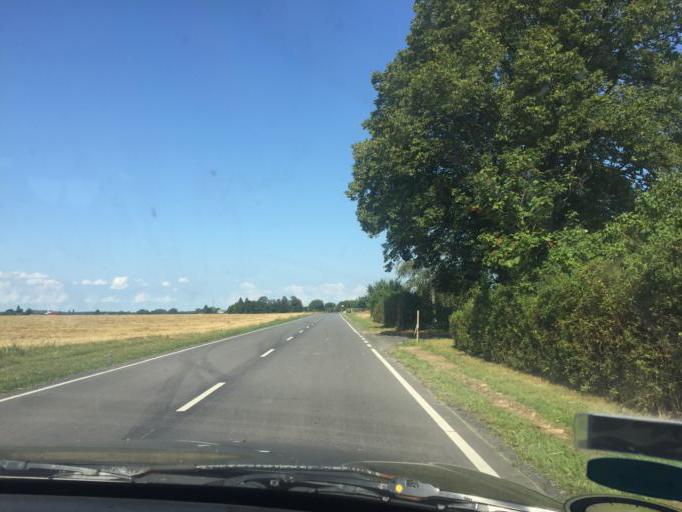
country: DK
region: Zealand
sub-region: Guldborgsund Kommune
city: Sakskobing
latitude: 54.7936
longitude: 11.5695
